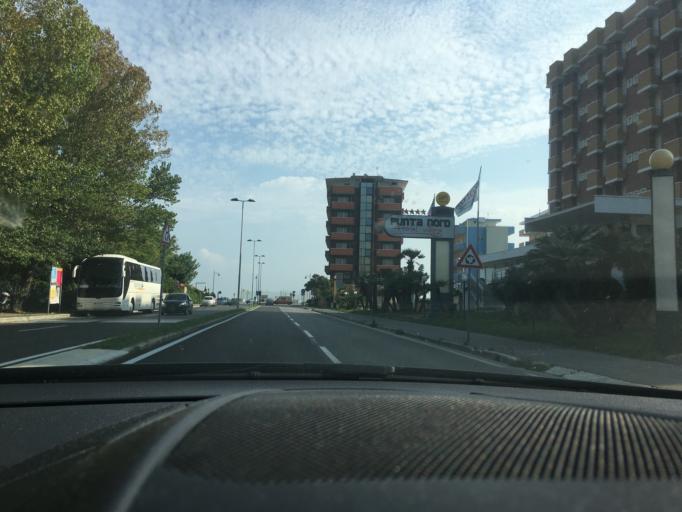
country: IT
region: Emilia-Romagna
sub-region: Provincia di Rimini
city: Bellaria-Igea Marina
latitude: 44.1124
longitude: 12.5034
